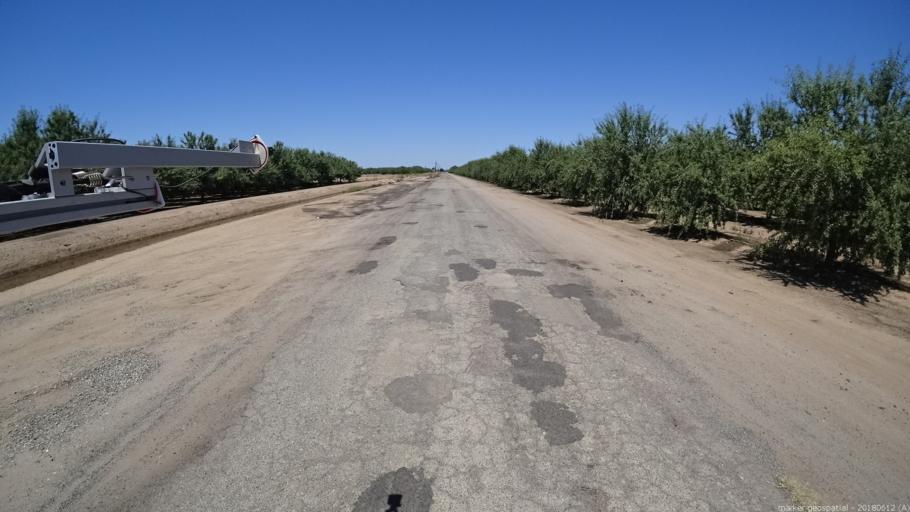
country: US
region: California
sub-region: Madera County
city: Chowchilla
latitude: 37.0593
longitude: -120.2659
